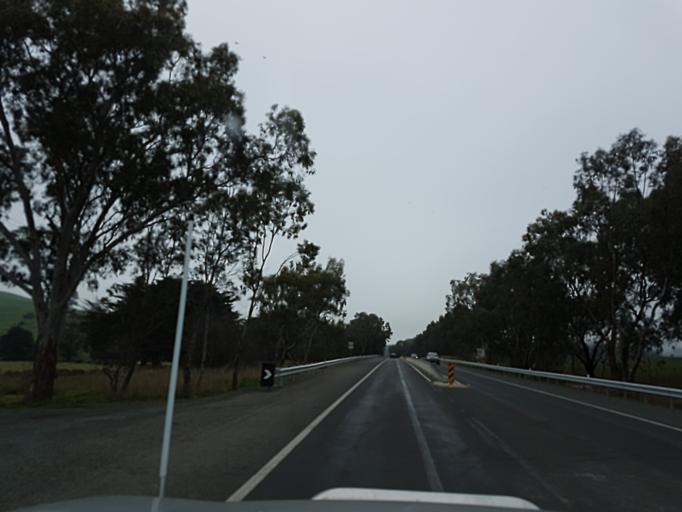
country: AU
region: Victoria
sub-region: Murrindindi
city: Alexandra
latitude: -37.2108
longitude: 145.4505
